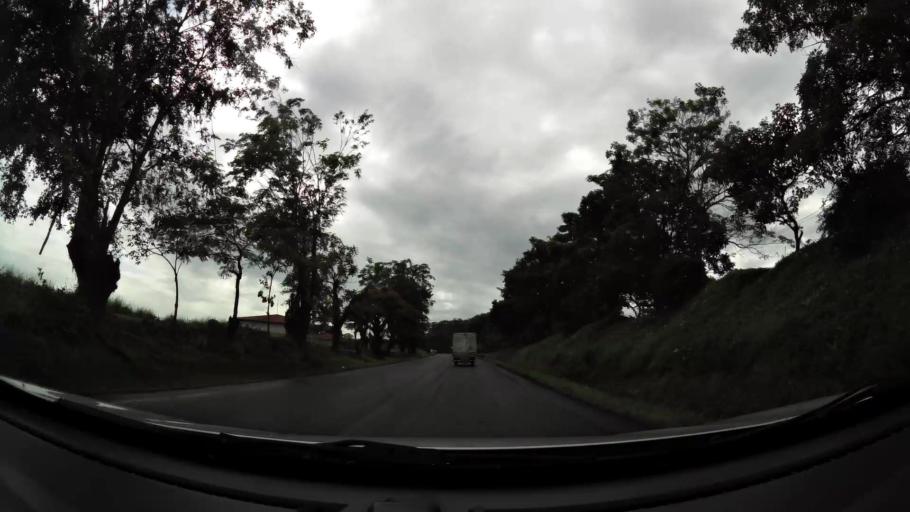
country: CR
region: Limon
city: Pocora
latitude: 10.1566
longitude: -83.5955
